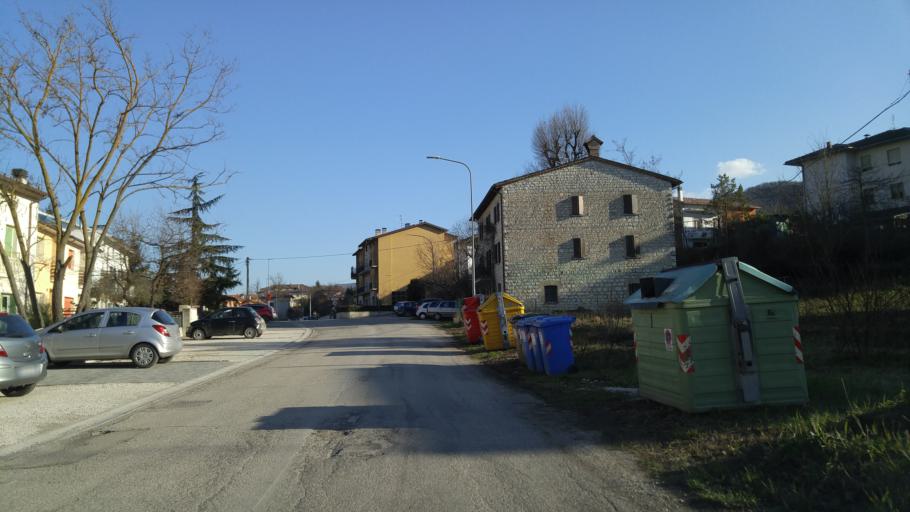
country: IT
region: The Marches
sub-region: Provincia di Pesaro e Urbino
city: Cagli
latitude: 43.5477
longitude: 12.6577
